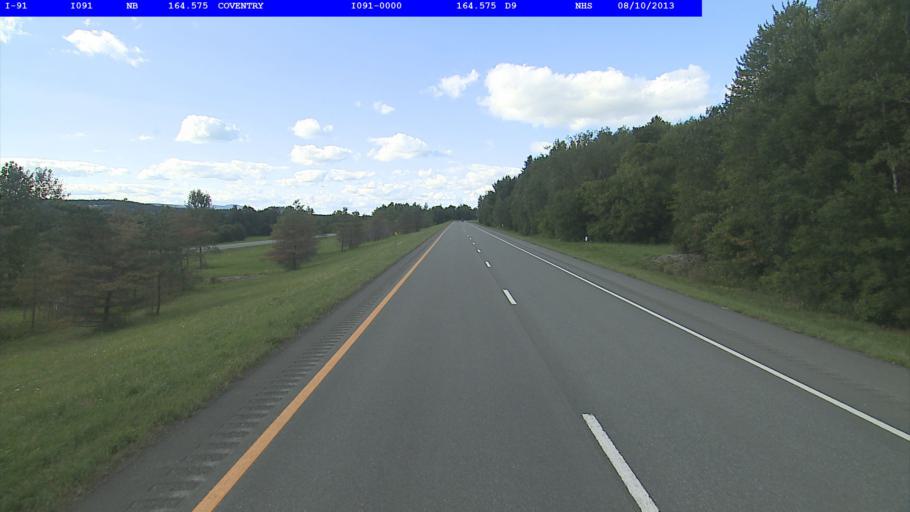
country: US
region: Vermont
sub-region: Orleans County
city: Newport
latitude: 44.8488
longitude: -72.1931
